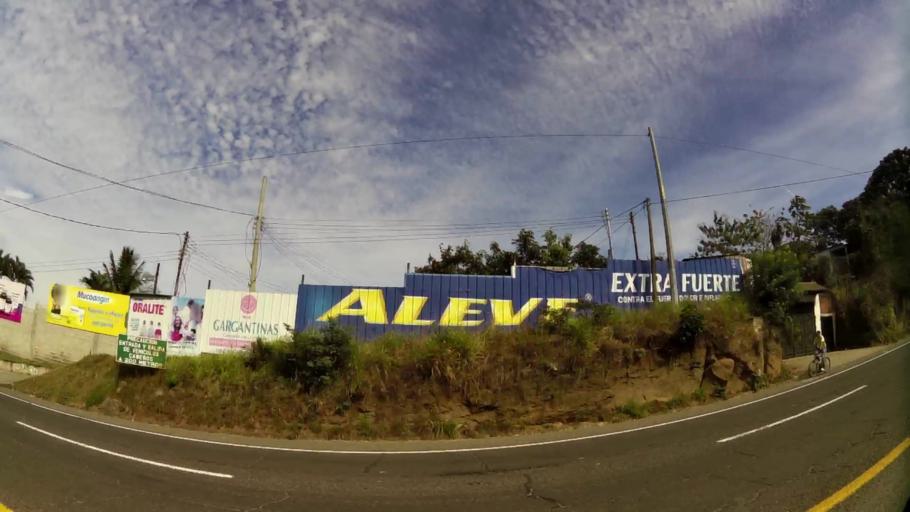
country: SV
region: Santa Ana
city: Chalchuapa
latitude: 13.9839
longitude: -89.6906
